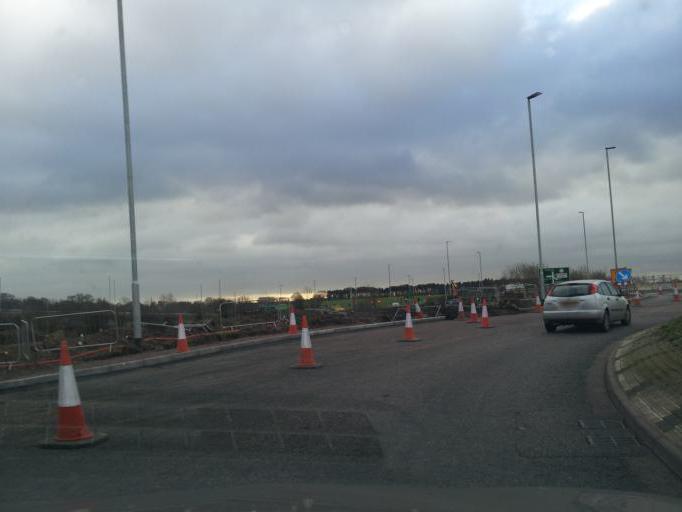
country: GB
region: England
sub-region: Norfolk
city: Surlingham
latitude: 52.6271
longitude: 1.3789
